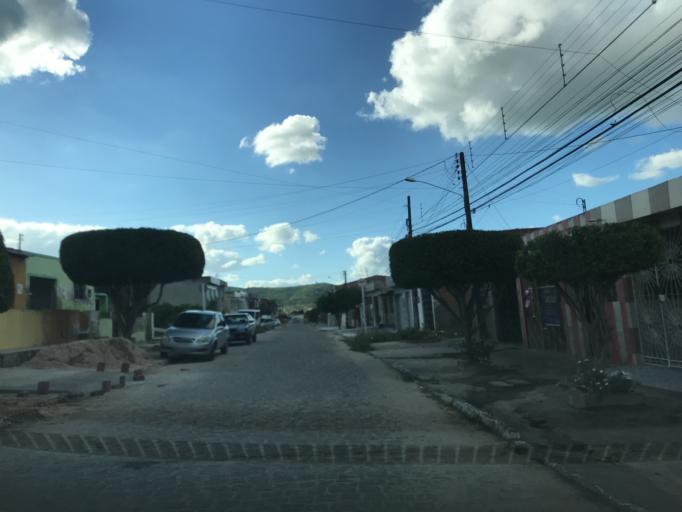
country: BR
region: Pernambuco
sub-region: Bezerros
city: Bezerros
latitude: -8.2448
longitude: -35.7579
